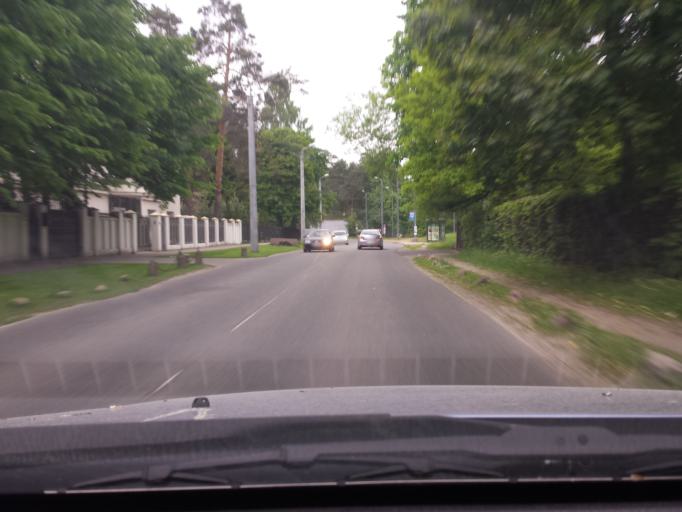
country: LV
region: Riga
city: Jaunciems
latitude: 57.0059
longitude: 24.1661
